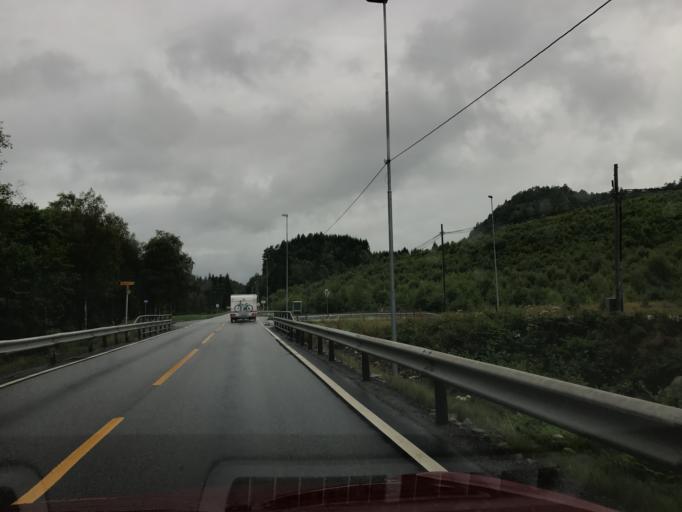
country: NO
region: Vest-Agder
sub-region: Lyngdal
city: Lyngdal
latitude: 58.1497
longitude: 7.1558
